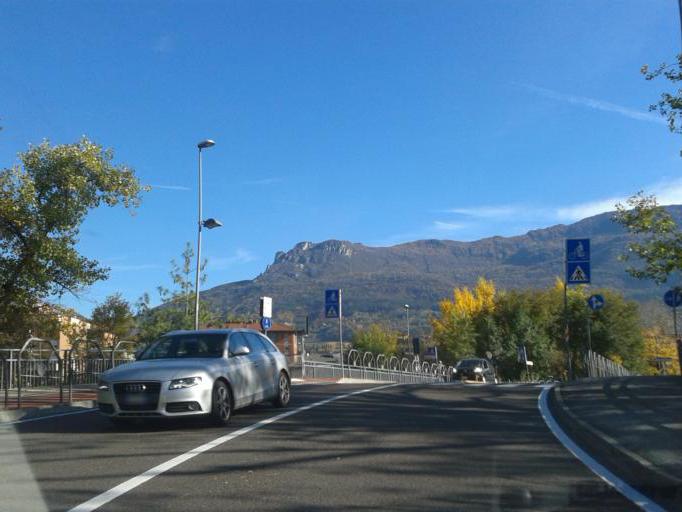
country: IT
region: Trentino-Alto Adige
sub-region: Provincia di Trento
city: Trento
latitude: 46.0528
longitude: 11.1210
